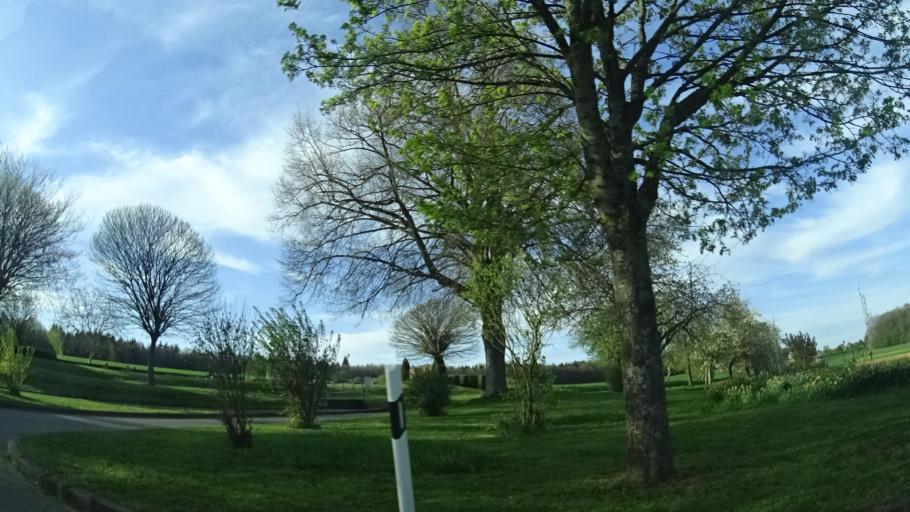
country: DE
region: Baden-Wuerttemberg
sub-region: Karlsruhe Region
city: Limbach
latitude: 49.4857
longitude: 9.2442
